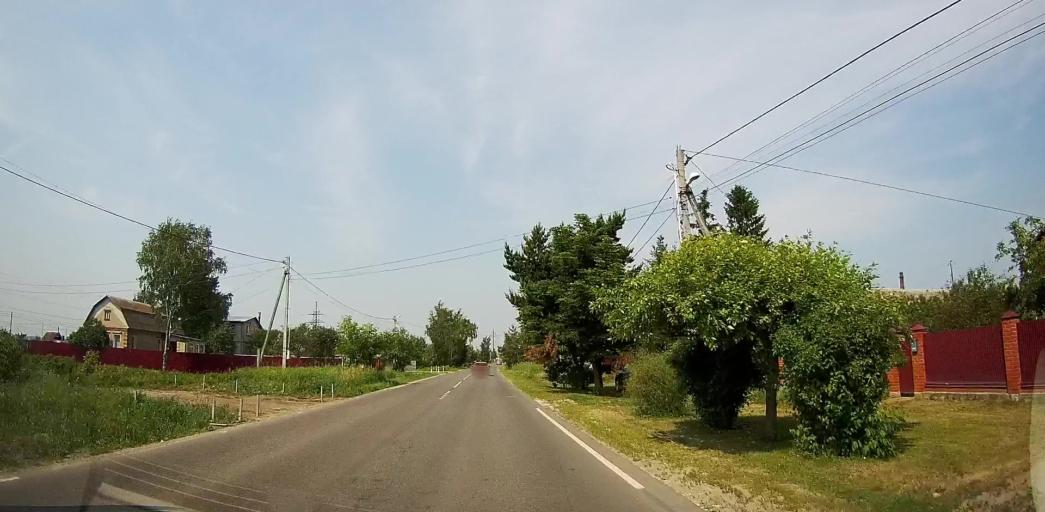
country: RU
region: Moskovskaya
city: Malyshevo
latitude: 55.5015
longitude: 38.3304
